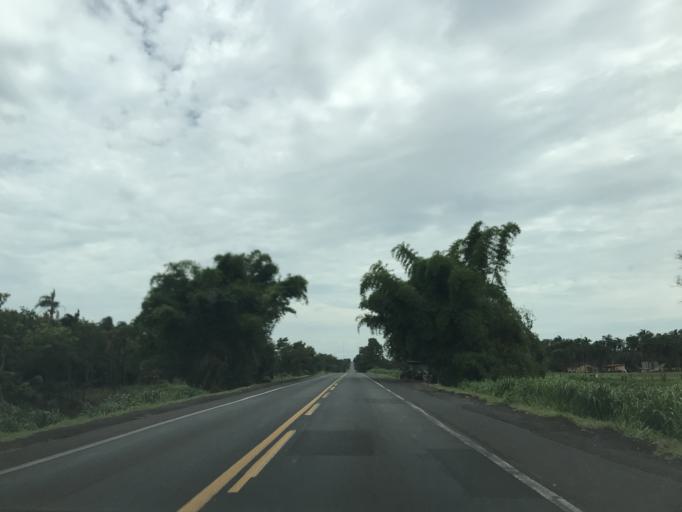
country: BR
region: Minas Gerais
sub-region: Frutal
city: Frutal
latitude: -20.1662
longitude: -49.1129
